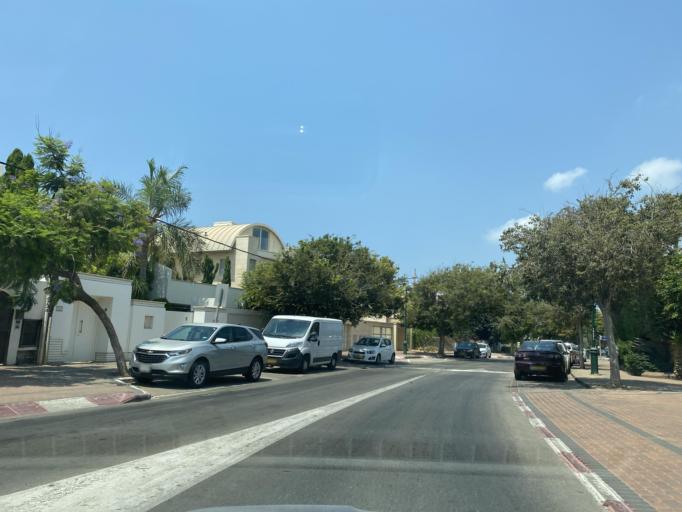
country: IL
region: Tel Aviv
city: Herzliya Pituah
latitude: 32.1736
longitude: 34.8037
